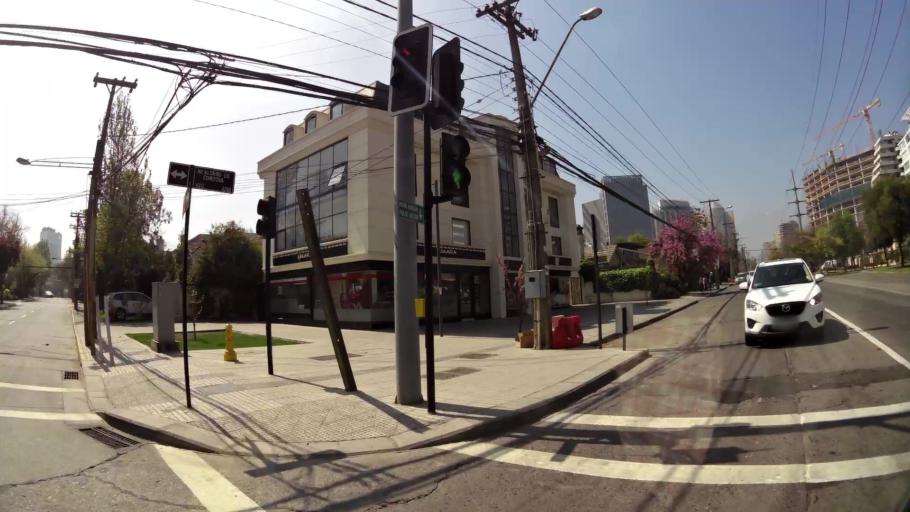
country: CL
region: Santiago Metropolitan
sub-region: Provincia de Santiago
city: Villa Presidente Frei, Nunoa, Santiago, Chile
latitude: -33.4031
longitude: -70.5897
